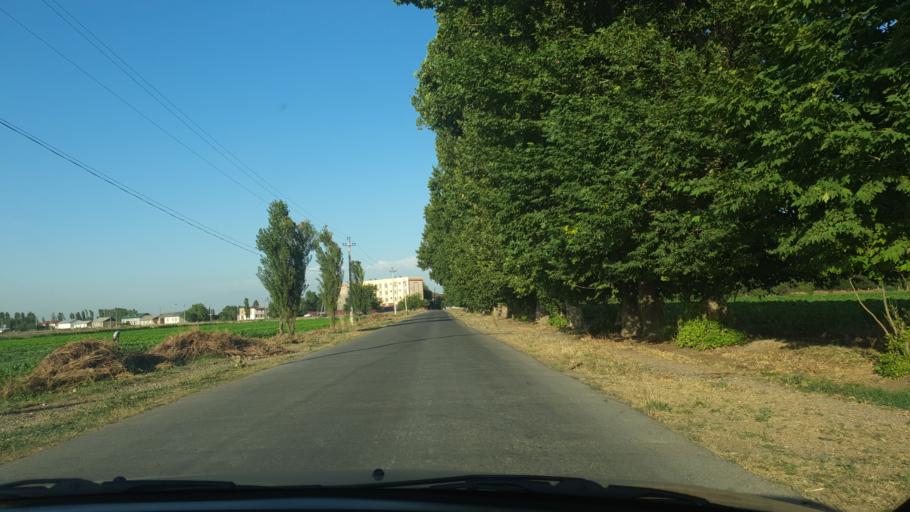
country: UZ
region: Toshkent
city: Tuytepa
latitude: 41.0865
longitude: 69.3502
